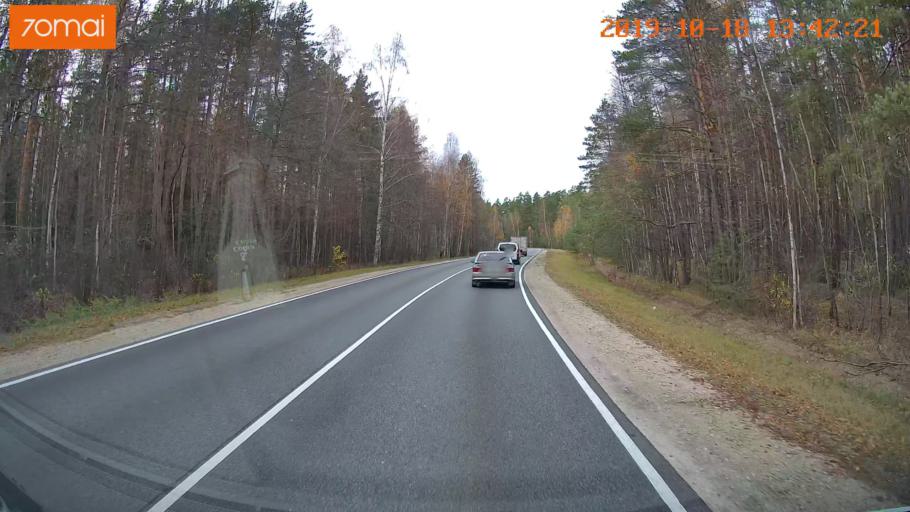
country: RU
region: Rjazan
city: Solotcha
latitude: 54.9254
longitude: 39.9911
